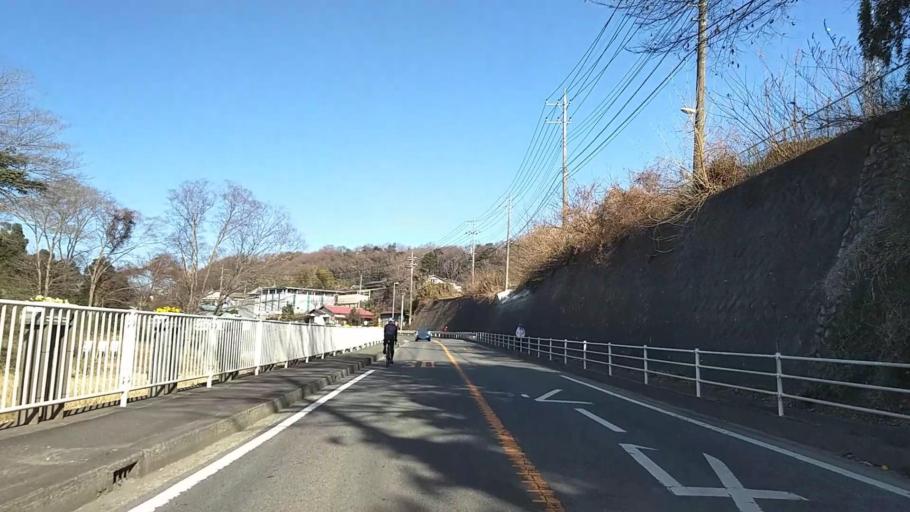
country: JP
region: Kanagawa
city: Atsugi
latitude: 35.4725
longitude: 139.3113
